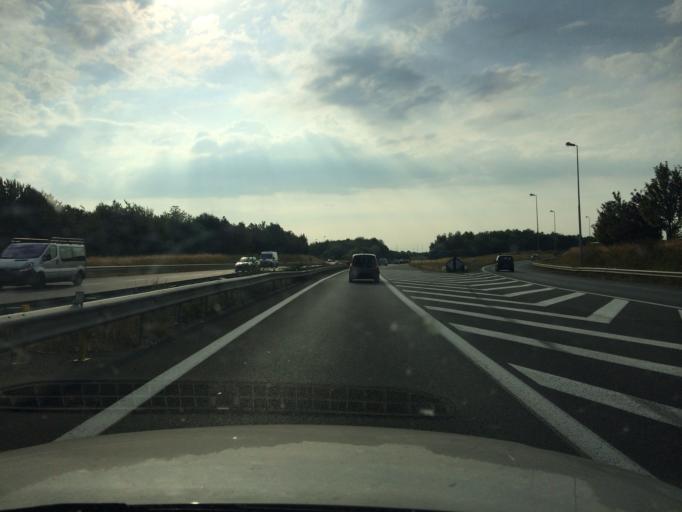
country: FR
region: Lower Normandy
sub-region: Departement du Calvados
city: Giberville
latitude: 49.1674
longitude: -0.2940
